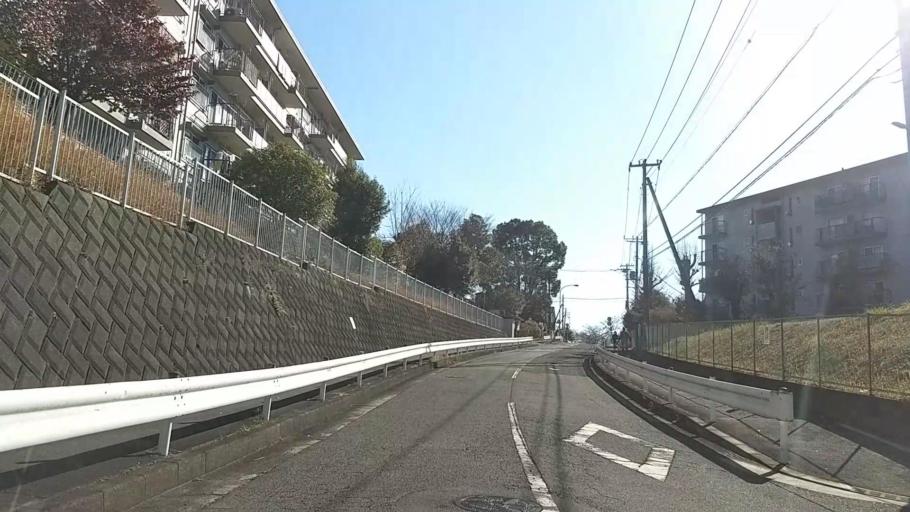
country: JP
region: Kanagawa
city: Hadano
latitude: 35.3851
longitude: 139.2185
